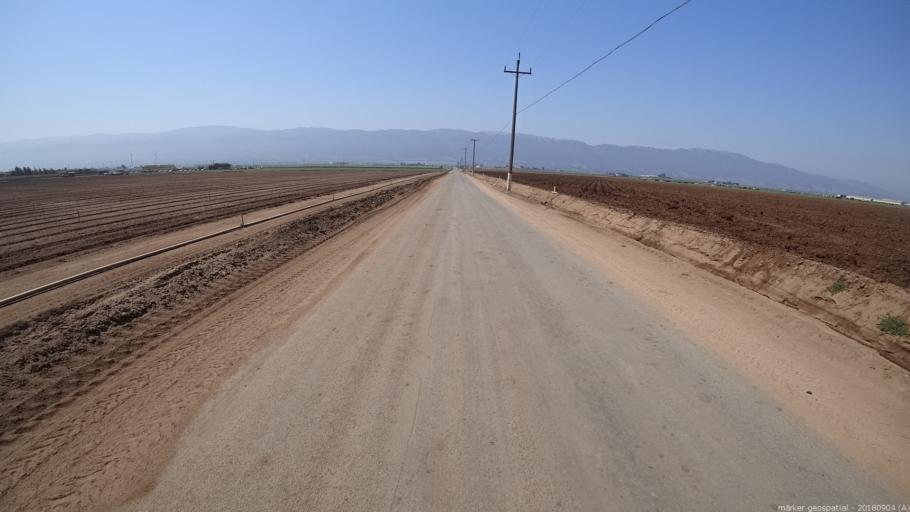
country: US
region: California
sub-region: Monterey County
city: Gonzales
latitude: 36.5314
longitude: -121.4488
